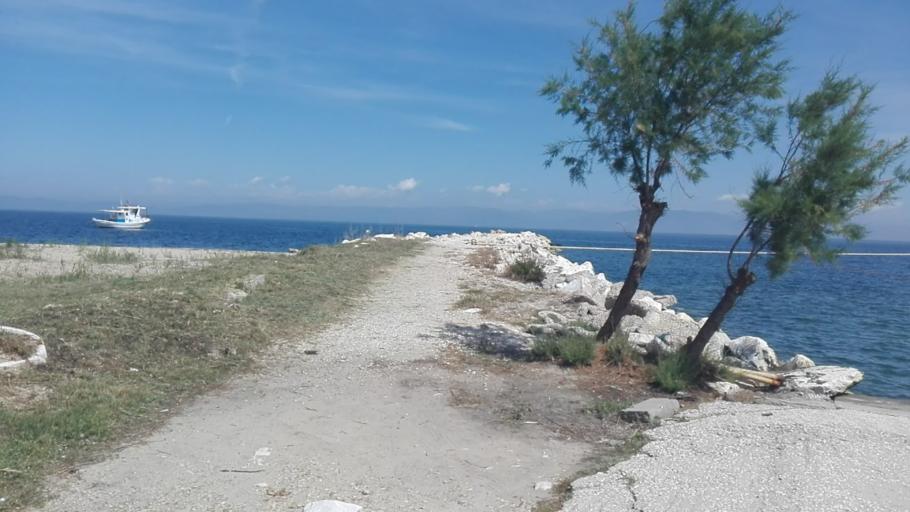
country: GR
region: East Macedonia and Thrace
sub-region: Nomos Kavalas
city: Prinos
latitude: 40.7595
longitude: 24.5759
